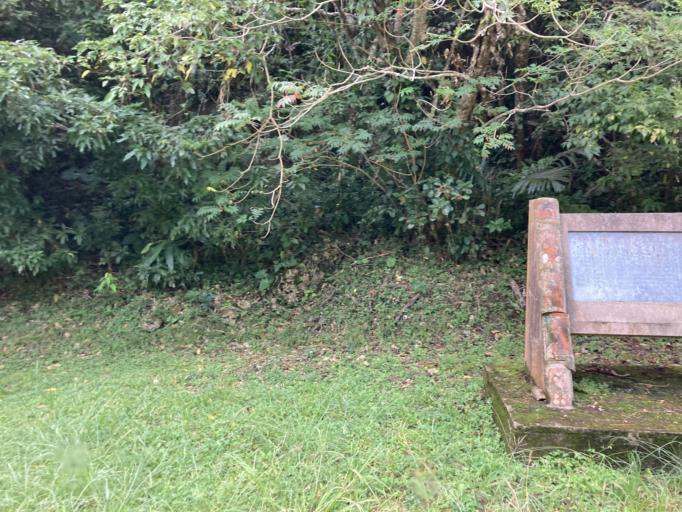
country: JP
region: Okinawa
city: Ginowan
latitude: 26.1606
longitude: 127.8121
